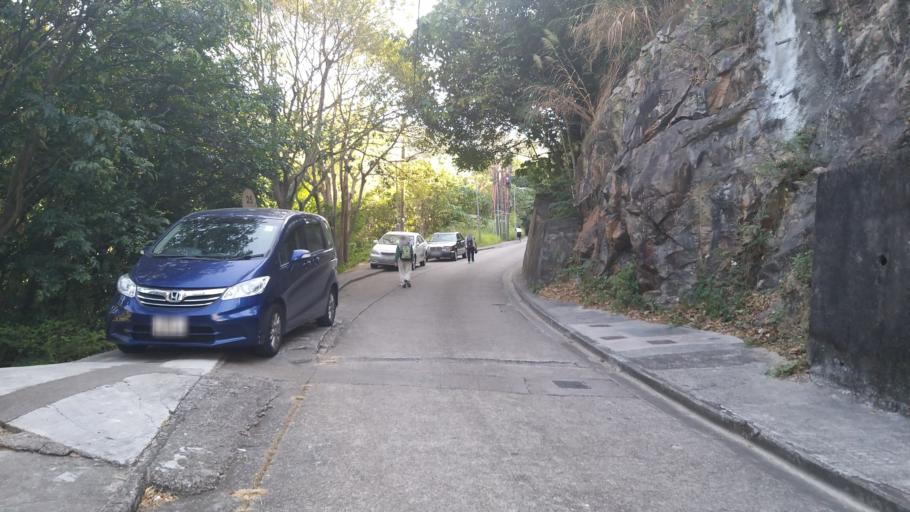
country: HK
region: Tuen Mun
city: Tuen Mun
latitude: 22.4073
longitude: 113.9855
